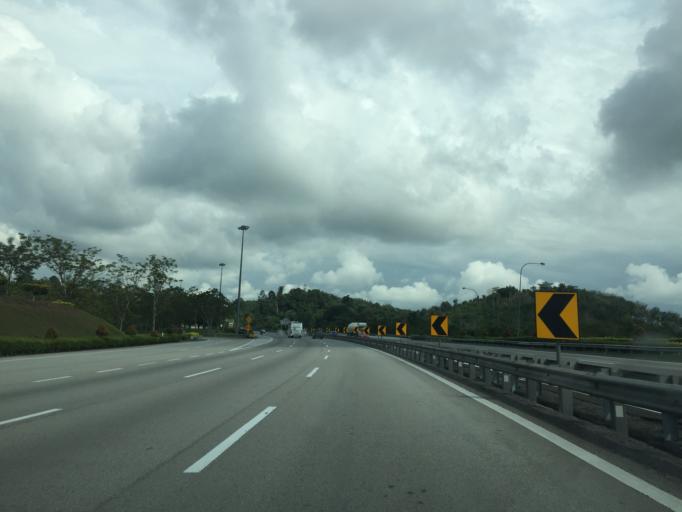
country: MY
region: Selangor
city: Batang Berjuntai
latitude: 3.5779
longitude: 101.5248
